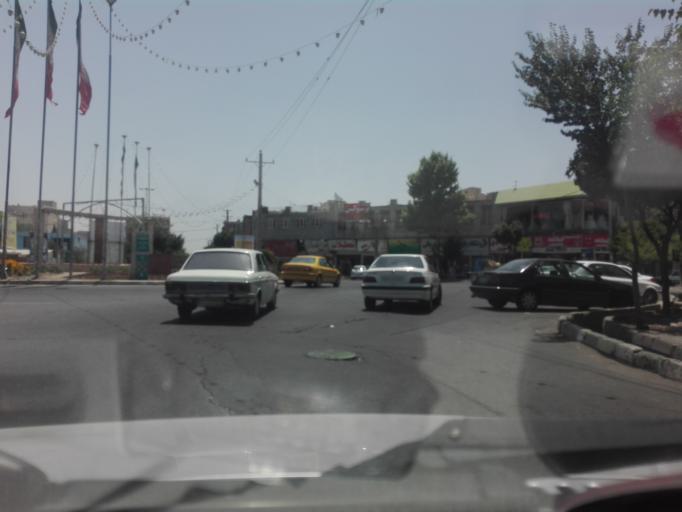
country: IR
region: Tehran
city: Shahre Jadide Andisheh
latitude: 35.7336
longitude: 50.9907
